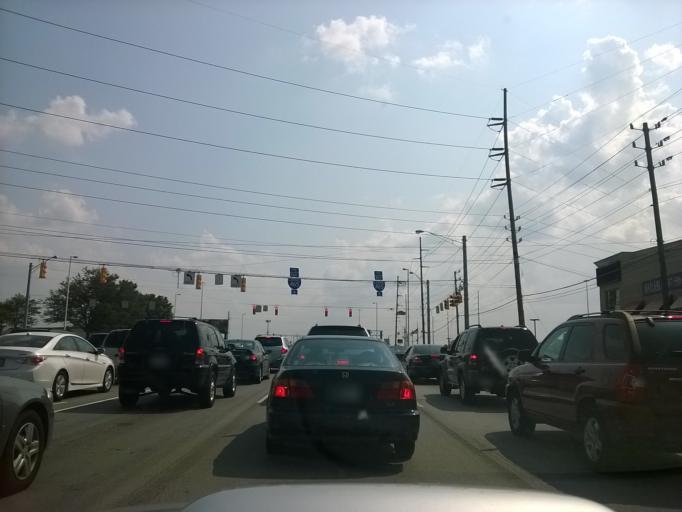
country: US
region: Indiana
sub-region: Hamilton County
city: Fishers
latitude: 39.9129
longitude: -86.0749
